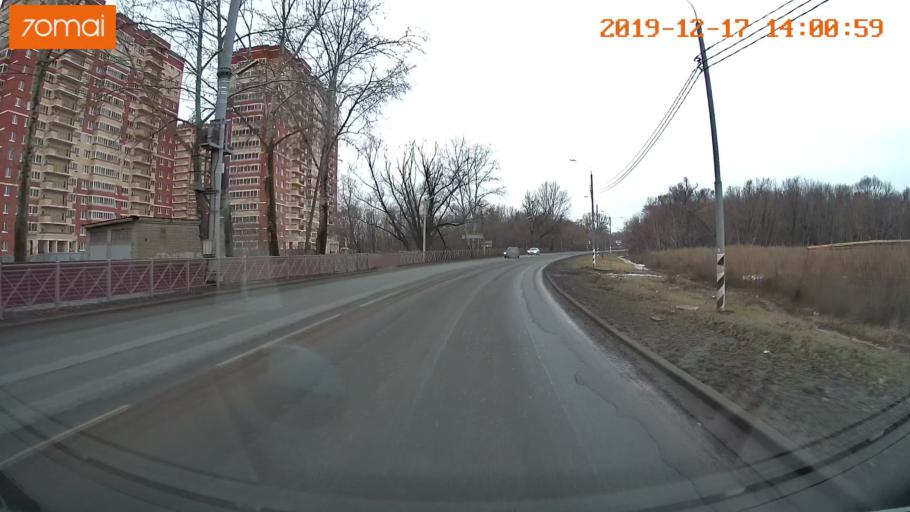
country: RU
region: Rjazan
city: Ryazan'
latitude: 54.6181
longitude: 39.6647
